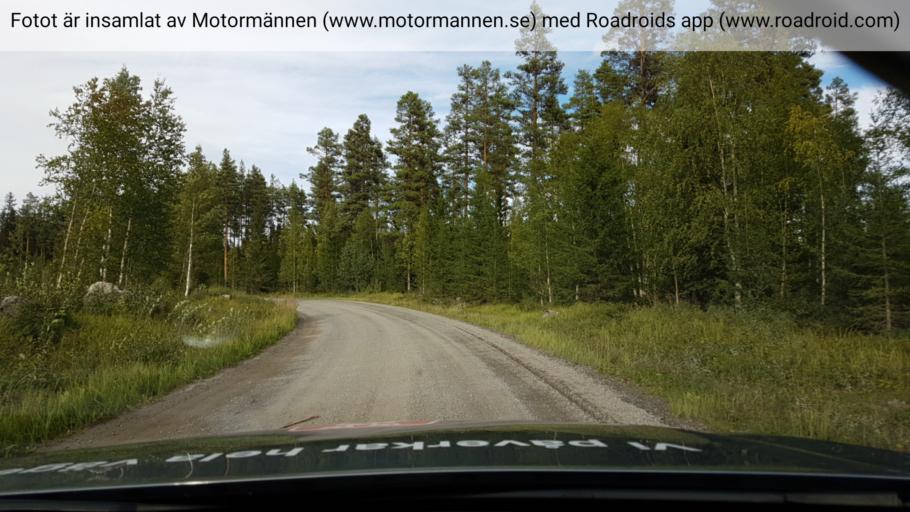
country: SE
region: Jaemtland
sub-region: Braecke Kommun
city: Braecke
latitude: 63.2411
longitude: 15.3690
